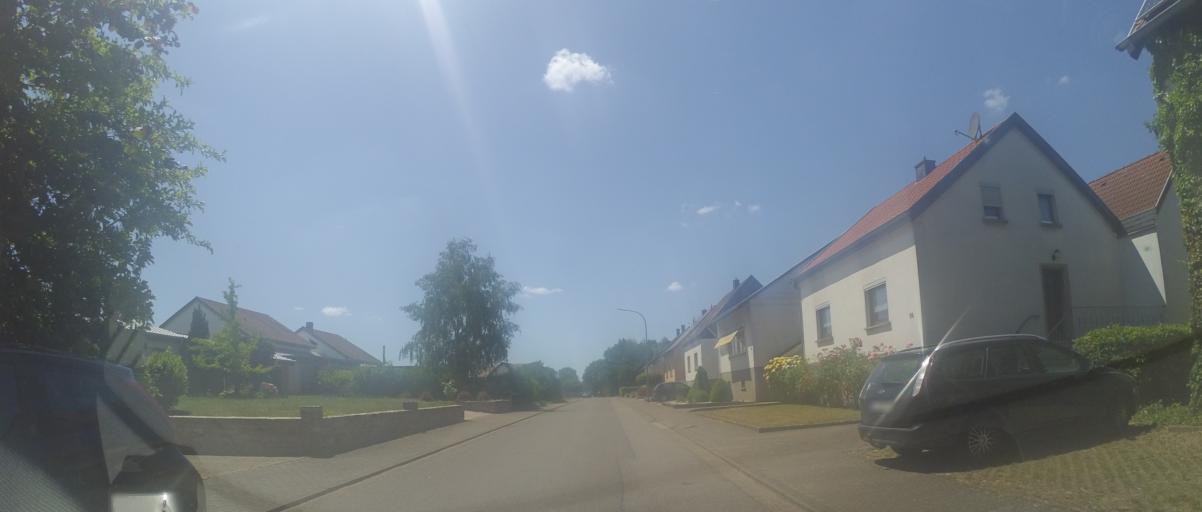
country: DE
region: Saarland
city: Heusweiler
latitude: 49.3422
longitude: 6.8889
